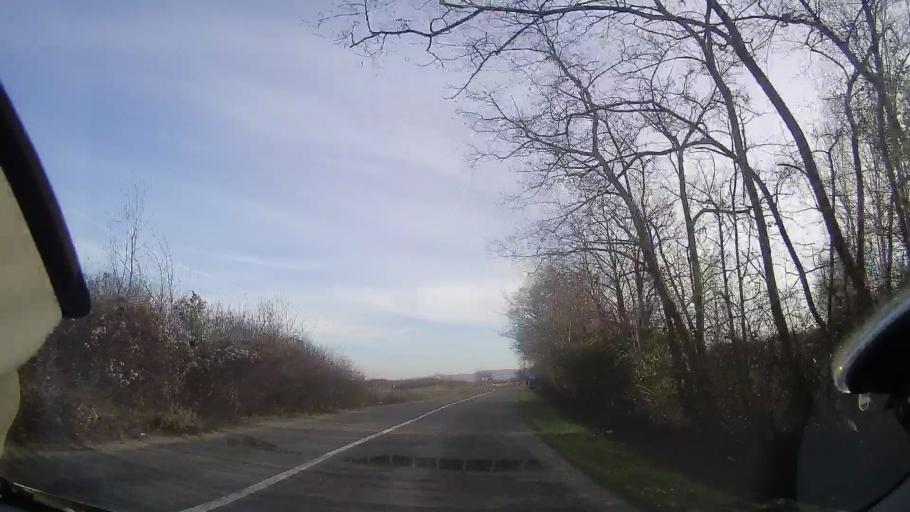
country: RO
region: Bihor
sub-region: Comuna Tileagd
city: Tileagd
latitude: 47.0662
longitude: 22.2157
